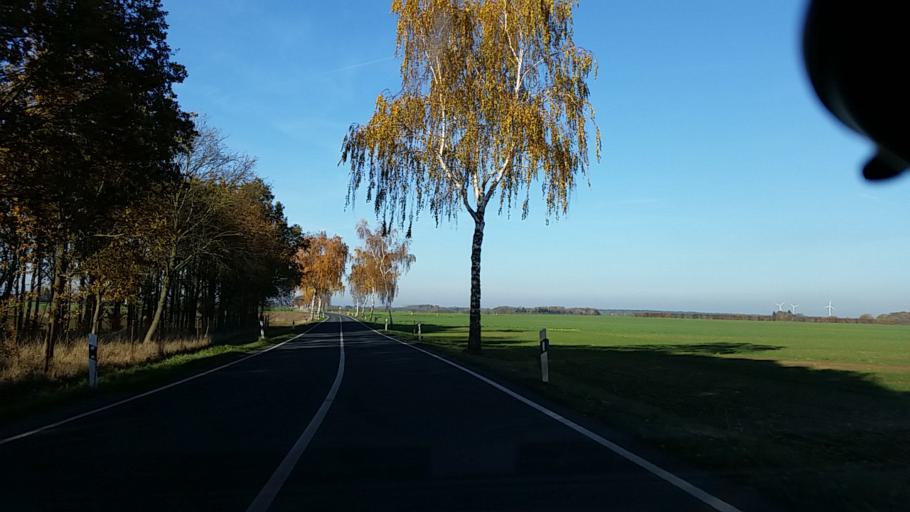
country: DE
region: Lower Saxony
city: Wittingen
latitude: 52.7454
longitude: 10.7336
